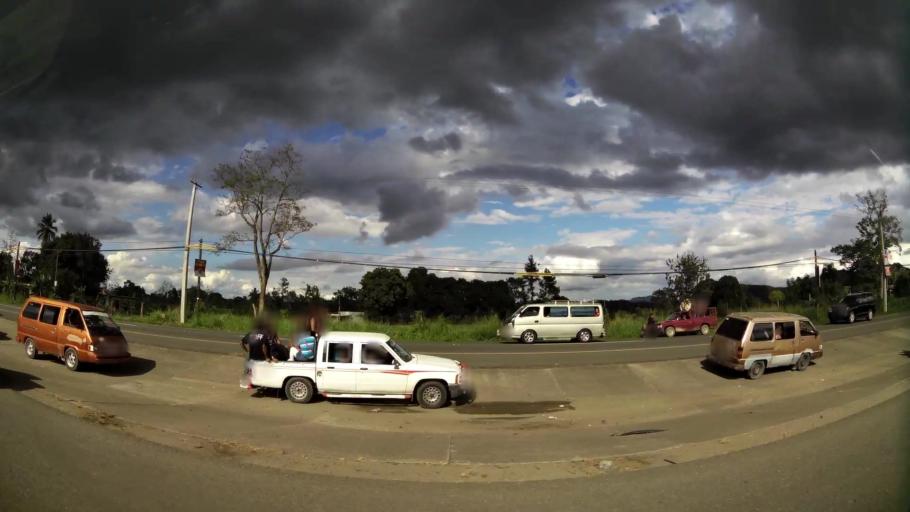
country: DO
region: Monsenor Nouel
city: Sabana del Puerto
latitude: 19.0016
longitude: -70.4383
